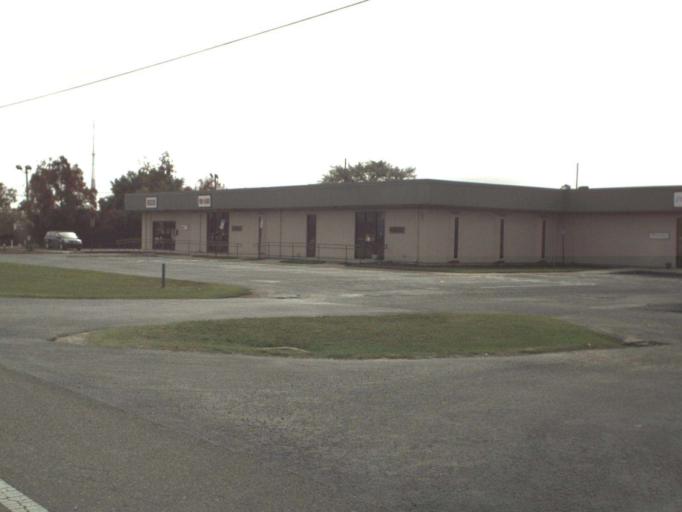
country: US
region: Florida
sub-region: Escambia County
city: Brent
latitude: 30.4830
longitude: -87.2565
